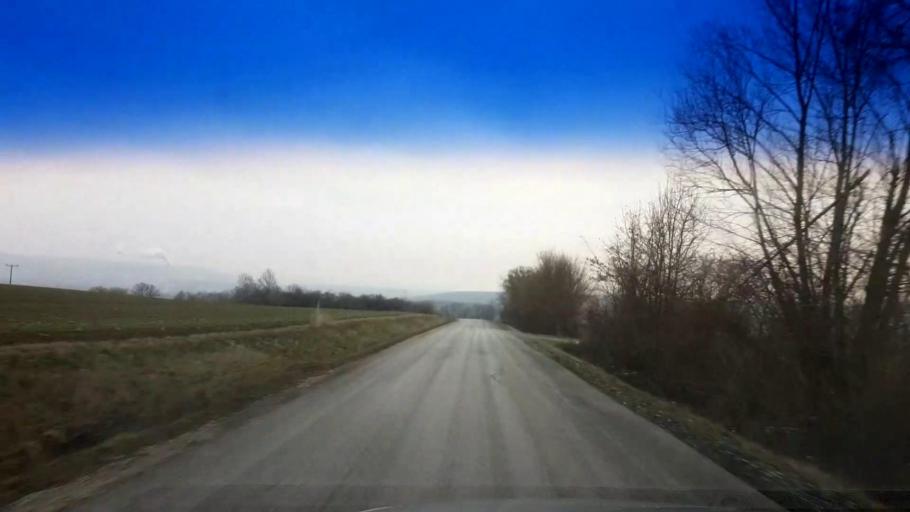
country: DE
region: Bavaria
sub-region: Upper Franconia
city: Hallerndorf
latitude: 49.7747
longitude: 10.9877
